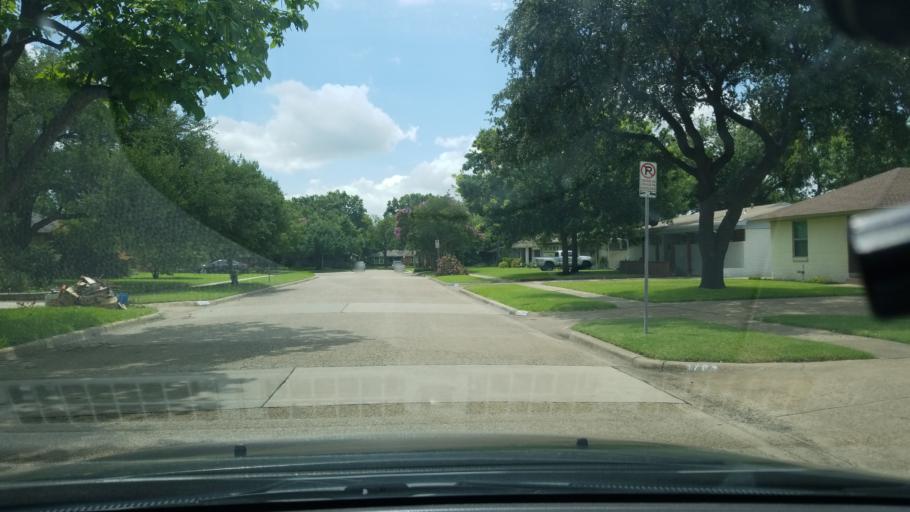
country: US
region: Texas
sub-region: Dallas County
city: Highland Park
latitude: 32.8267
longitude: -96.6921
